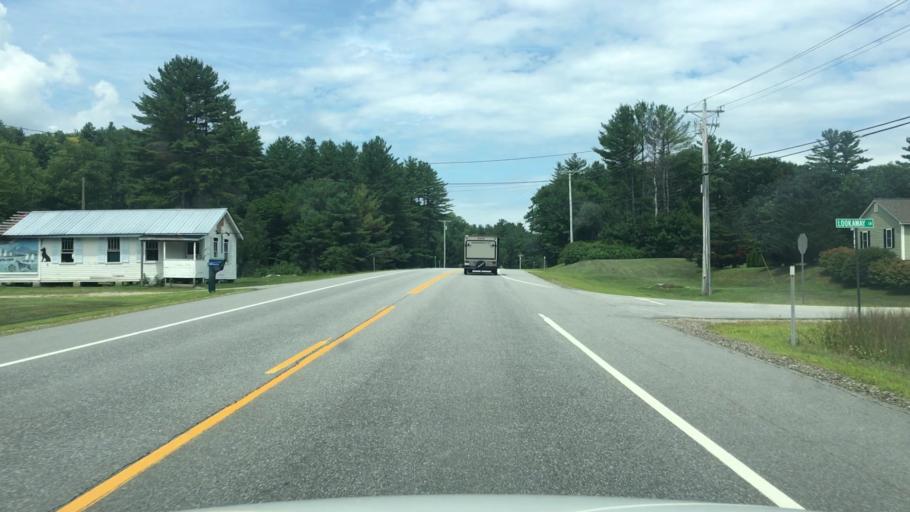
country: US
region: New Hampshire
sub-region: Grafton County
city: Rumney
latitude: 43.8347
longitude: -71.8999
